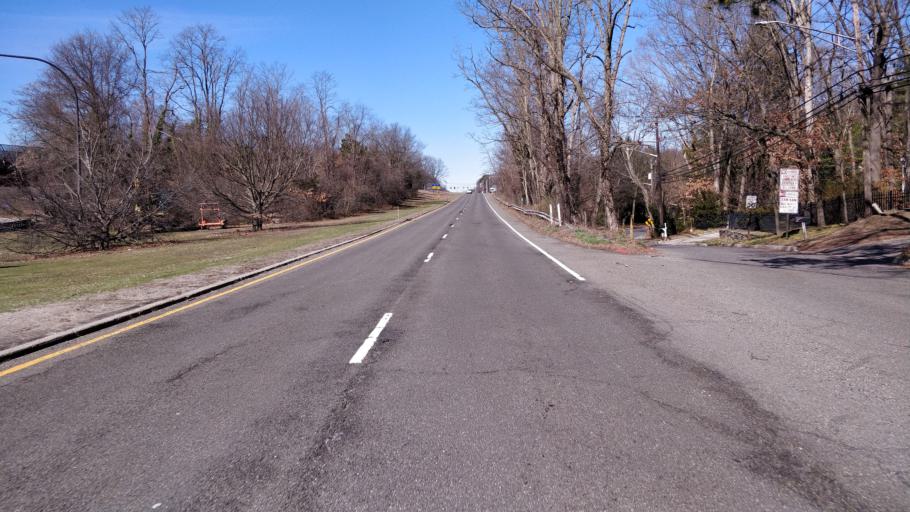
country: US
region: New York
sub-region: Suffolk County
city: Commack
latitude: 40.8304
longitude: -73.2530
